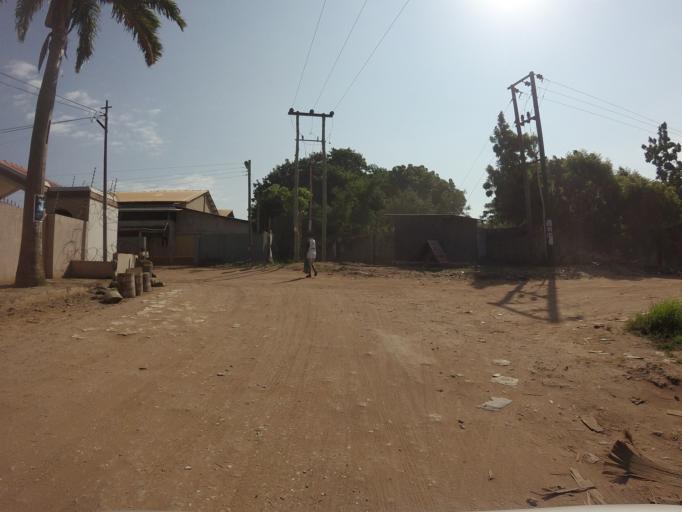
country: GH
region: Greater Accra
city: Dome
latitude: 5.6385
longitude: -0.2369
